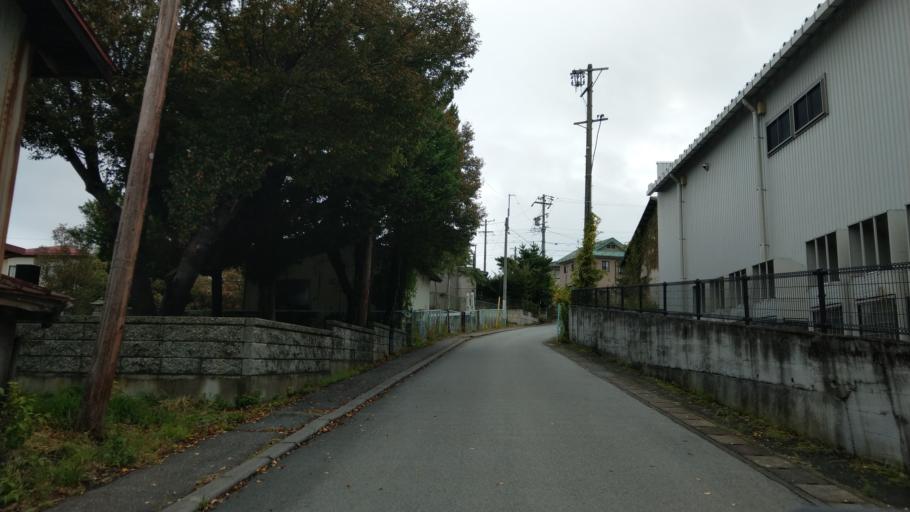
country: JP
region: Nagano
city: Komoro
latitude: 36.3181
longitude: 138.4364
